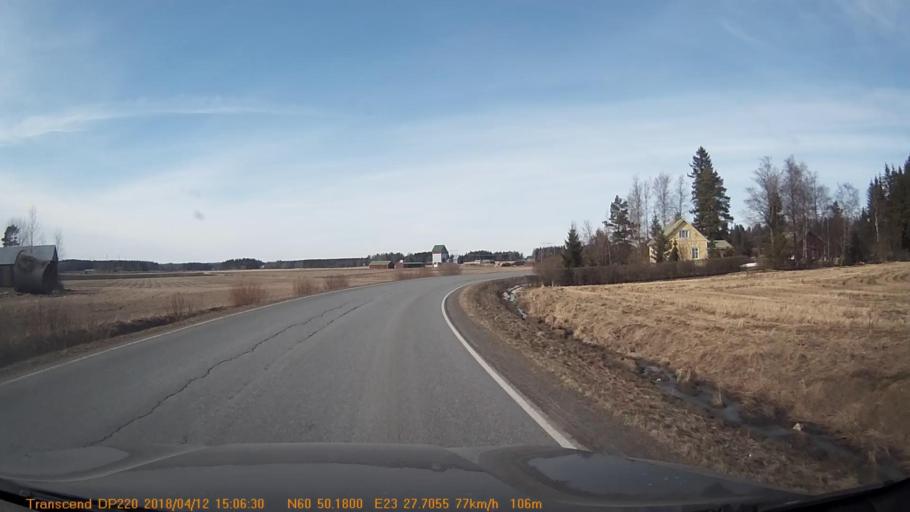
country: FI
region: Haeme
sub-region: Forssa
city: Jokioinen
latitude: 60.8367
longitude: 23.4613
